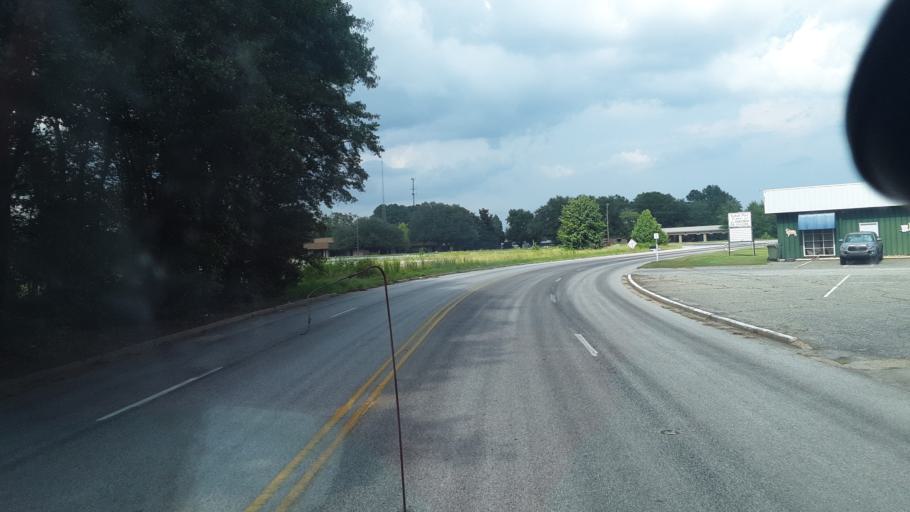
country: US
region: South Carolina
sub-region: Sumter County
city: Sumter
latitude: 33.9559
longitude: -80.3752
